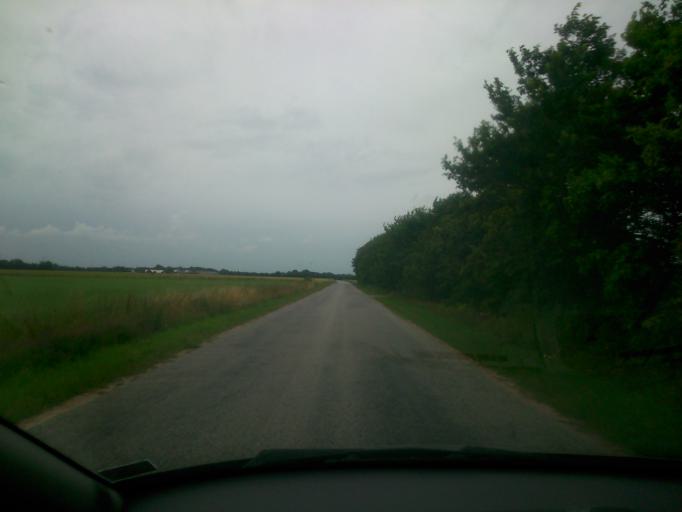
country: DK
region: South Denmark
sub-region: Esbjerg Kommune
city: Esbjerg
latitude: 55.5412
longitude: 8.4313
